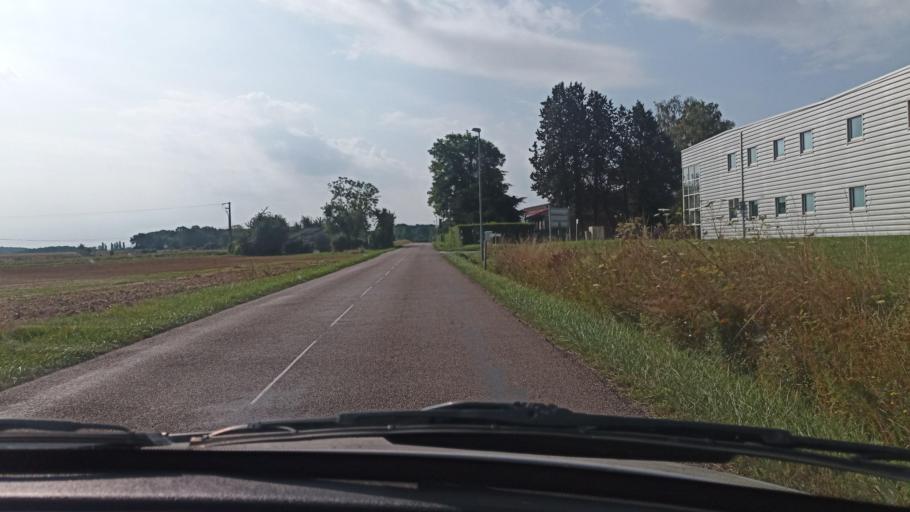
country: FR
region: Bourgogne
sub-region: Departement de l'Yonne
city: Saint-Valerien
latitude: 48.1949
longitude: 3.0875
